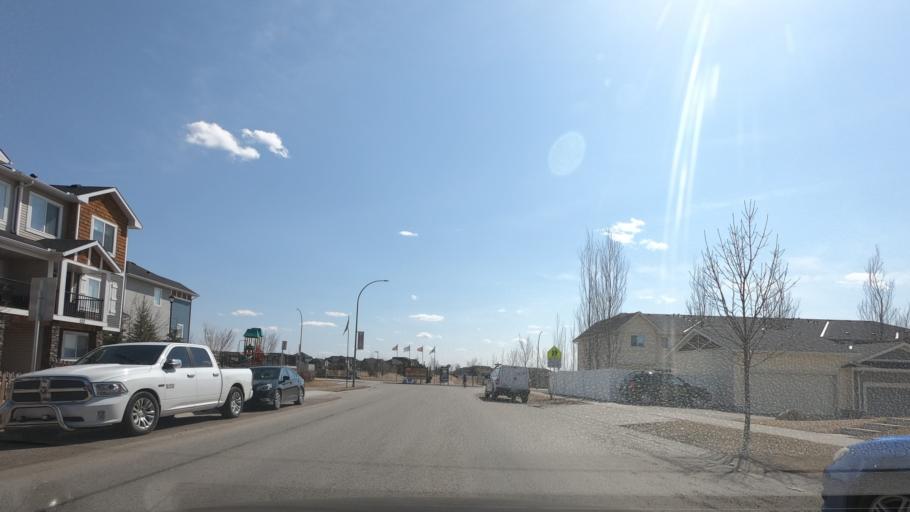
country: CA
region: Alberta
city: Airdrie
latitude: 51.2677
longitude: -113.9818
